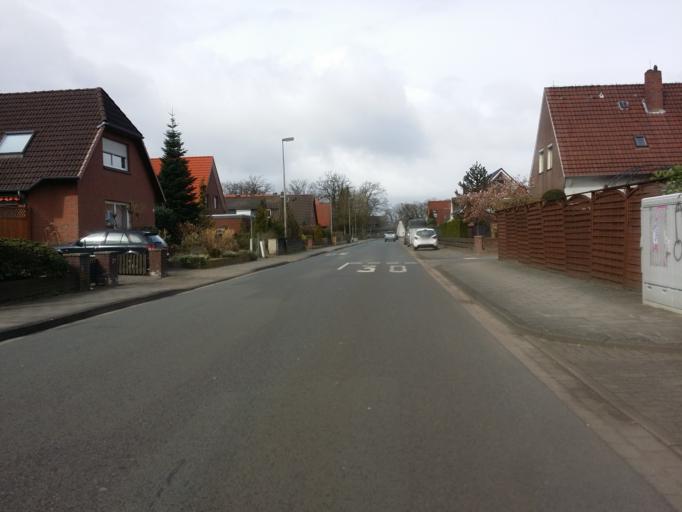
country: DE
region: Lower Saxony
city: Delmenhorst
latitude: 53.0197
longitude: 8.6501
